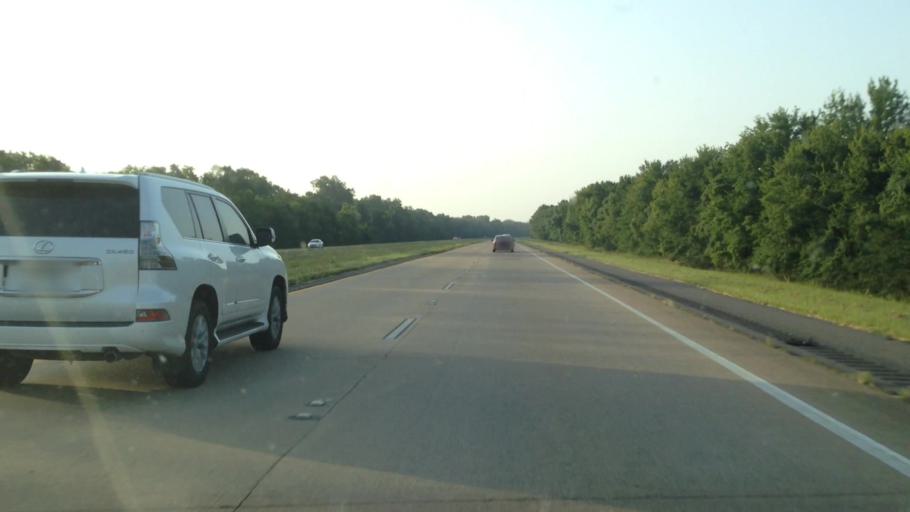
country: US
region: Louisiana
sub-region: Natchitoches Parish
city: Vienna Bend
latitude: 31.5512
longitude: -92.9708
